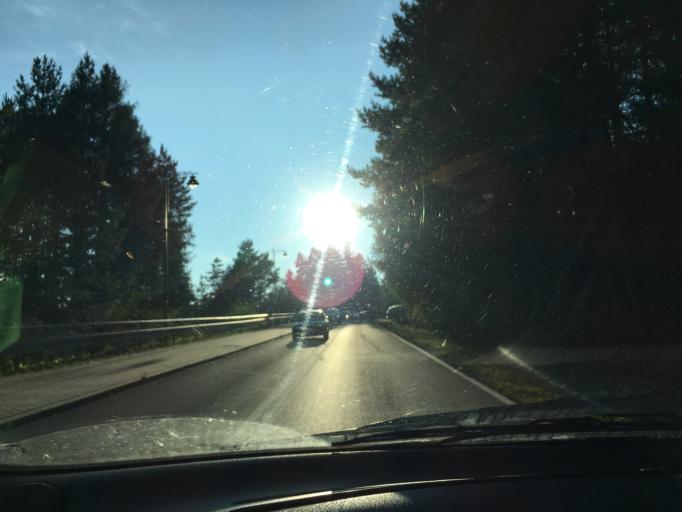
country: PL
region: Lesser Poland Voivodeship
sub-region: Powiat nowotarski
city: Niedzica
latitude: 49.4164
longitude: 20.3185
